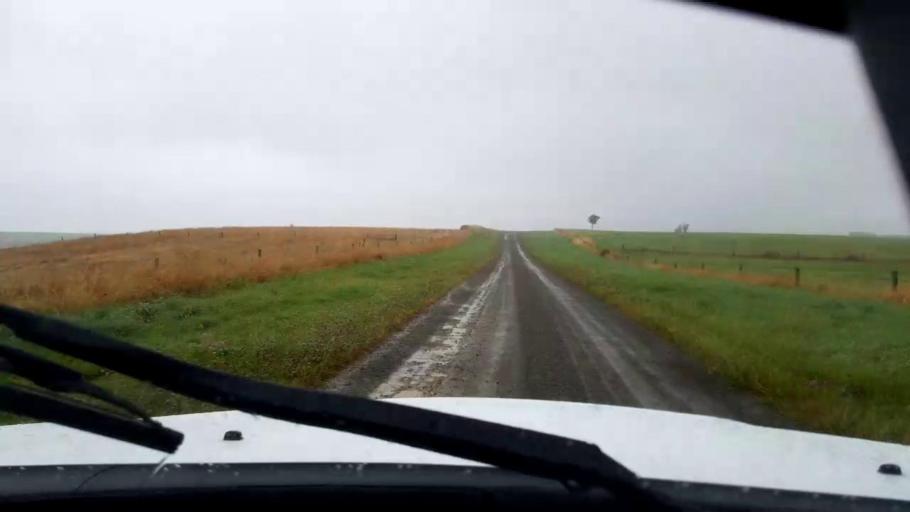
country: NZ
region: Canterbury
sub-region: Timaru District
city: Pleasant Point
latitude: -44.1678
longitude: 171.1671
